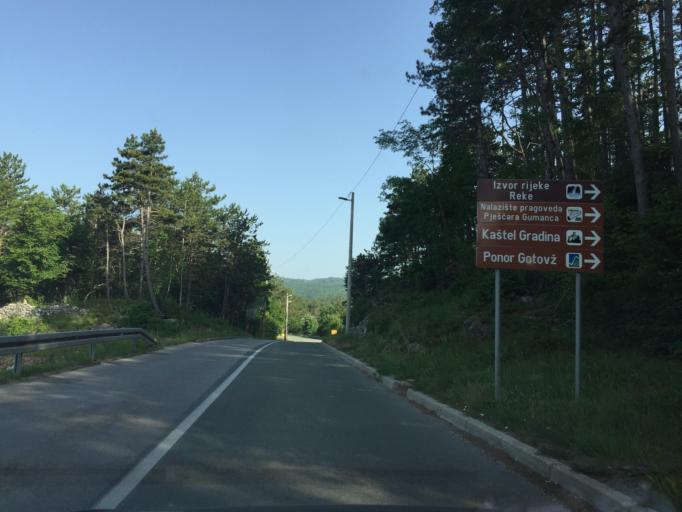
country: HR
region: Primorsko-Goranska
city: Klana
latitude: 45.4345
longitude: 14.3667
